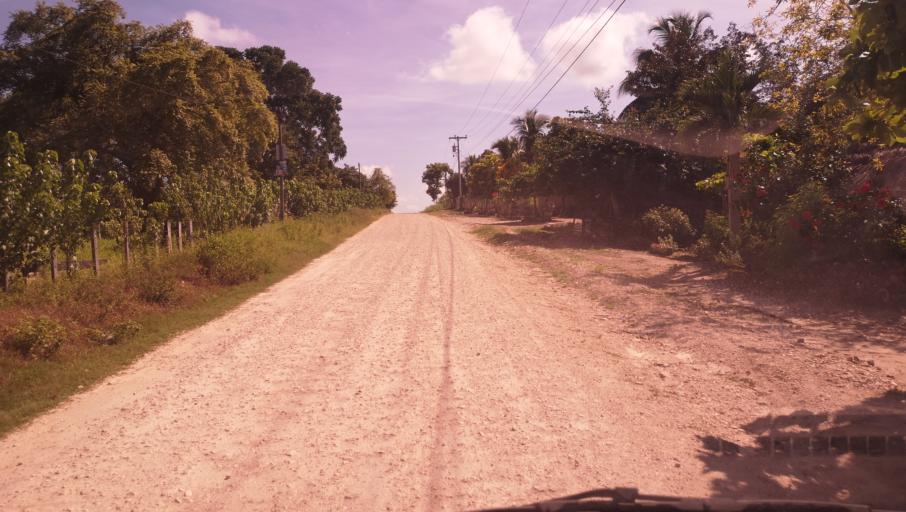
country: GT
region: Peten
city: Dolores
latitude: 16.7865
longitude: -89.3077
